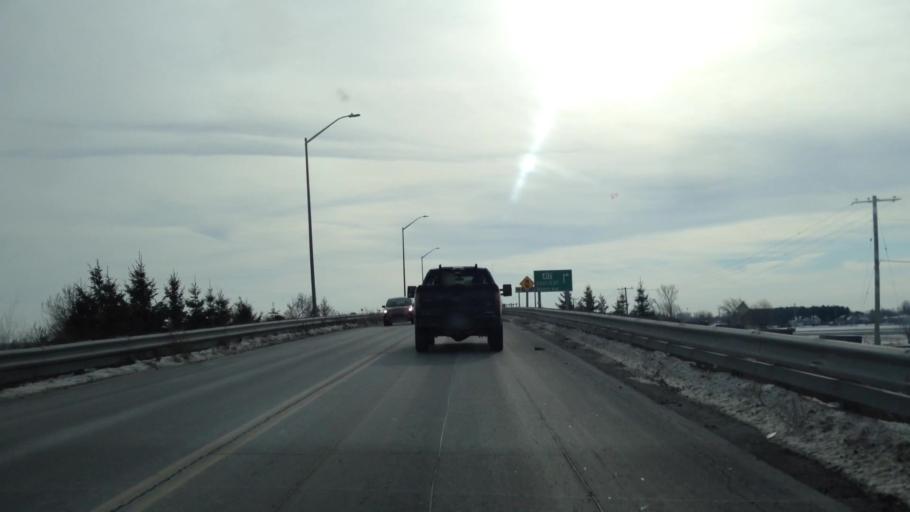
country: CA
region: Ontario
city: Casselman
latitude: 45.3041
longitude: -75.0808
